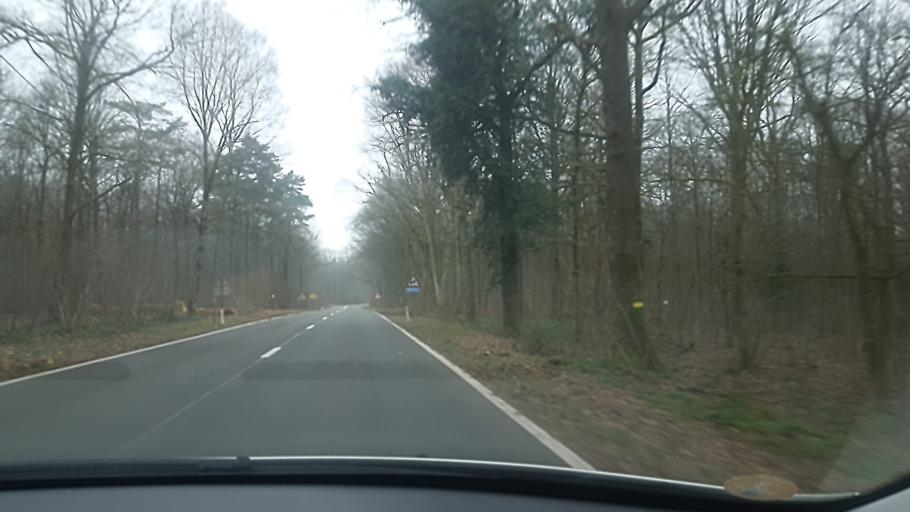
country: FR
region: Champagne-Ardenne
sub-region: Departement des Ardennes
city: Haybes
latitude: 50.0315
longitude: 4.6160
